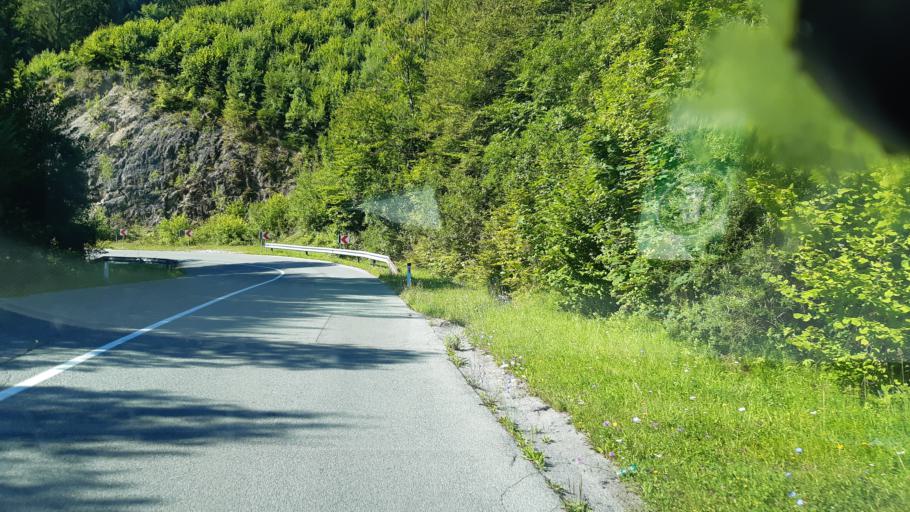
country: SI
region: Gornji Grad
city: Gornji Grad
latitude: 46.2144
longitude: 14.8073
